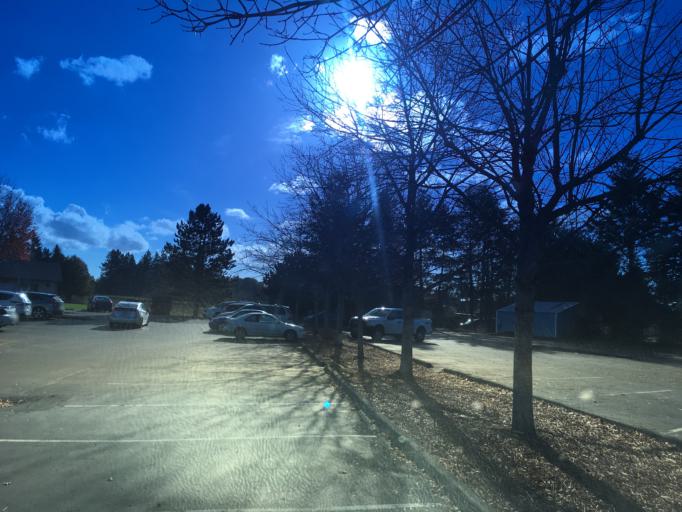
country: US
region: Oregon
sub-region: Multnomah County
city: Troutdale
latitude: 45.5063
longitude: -122.3784
